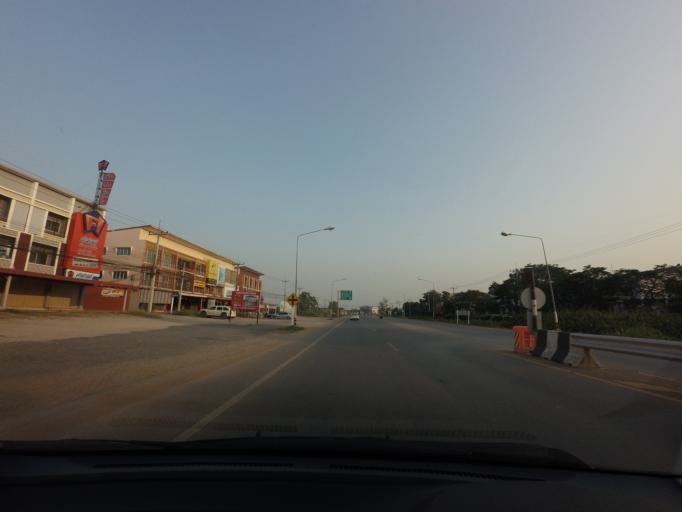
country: TH
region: Sukhothai
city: Sukhothai
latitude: 17.0137
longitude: 99.8348
